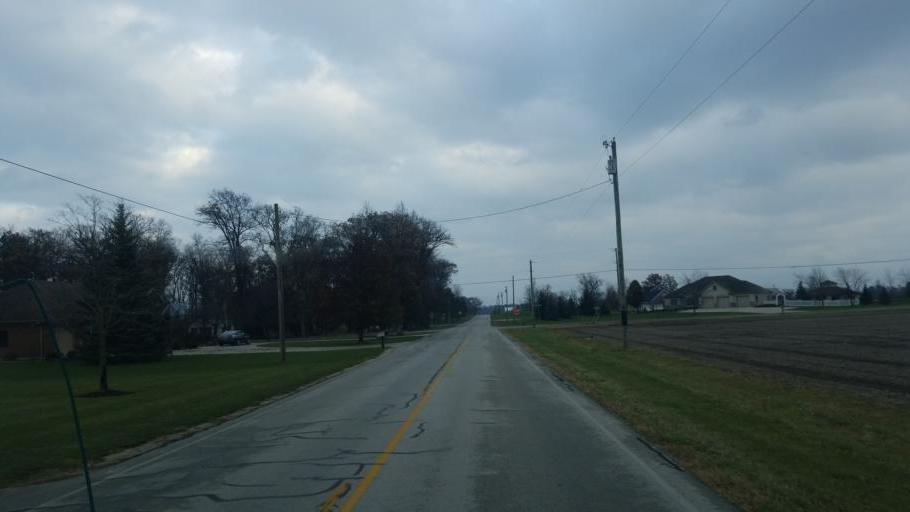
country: US
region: Ohio
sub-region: Mercer County
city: Coldwater
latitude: 40.5091
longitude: -84.6109
